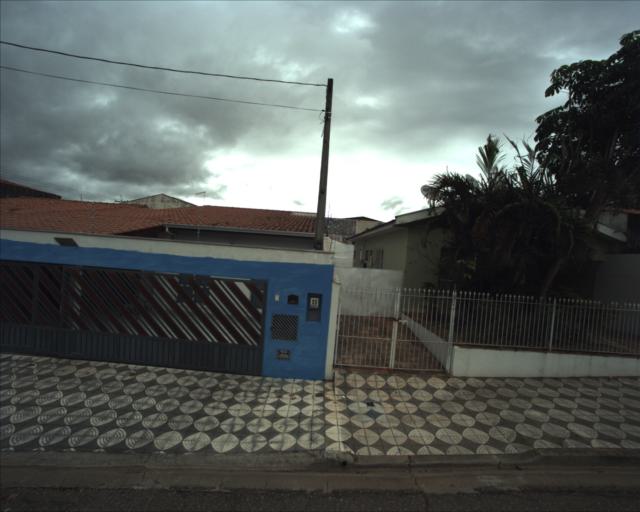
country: BR
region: Sao Paulo
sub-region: Sorocaba
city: Sorocaba
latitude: -23.4749
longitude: -47.4621
